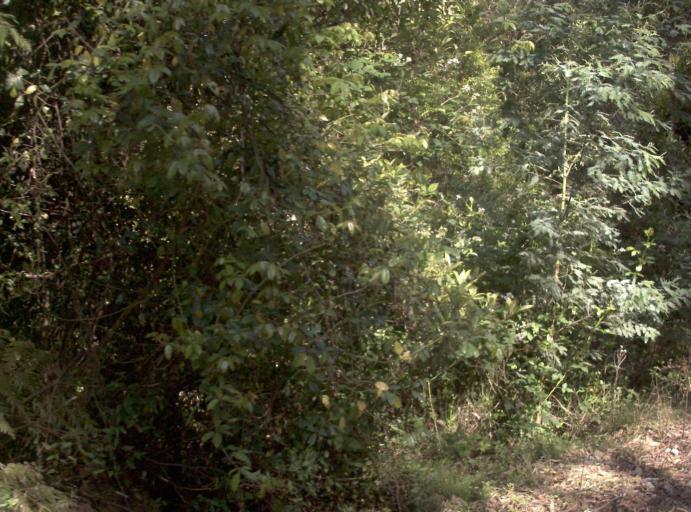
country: AU
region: Victoria
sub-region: East Gippsland
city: Lakes Entrance
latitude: -37.4256
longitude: 148.6022
